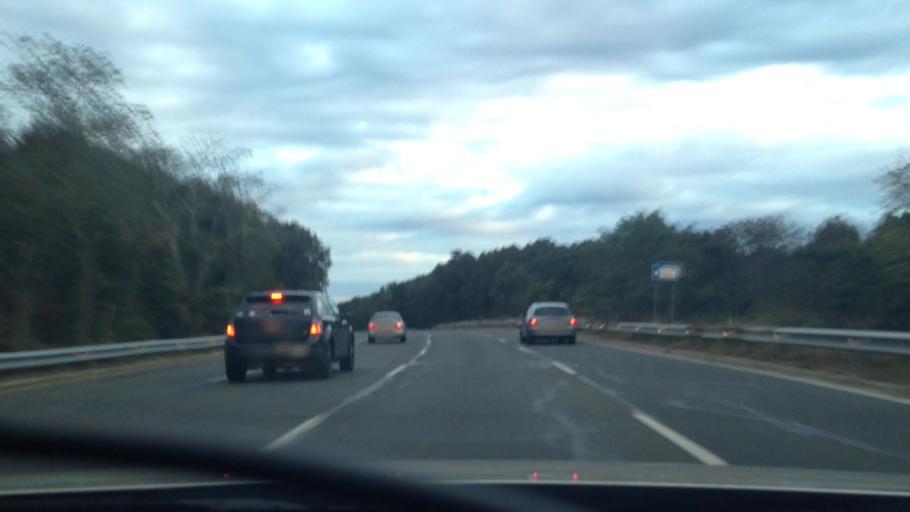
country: US
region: New York
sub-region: Suffolk County
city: Farmingville
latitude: 40.8484
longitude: -73.0171
